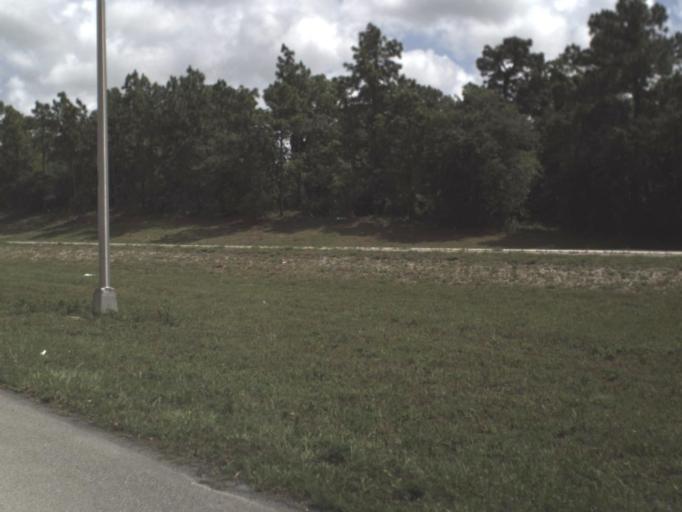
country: US
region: Florida
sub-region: Saint Johns County
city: Fruit Cove
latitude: 30.2058
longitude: -81.5517
